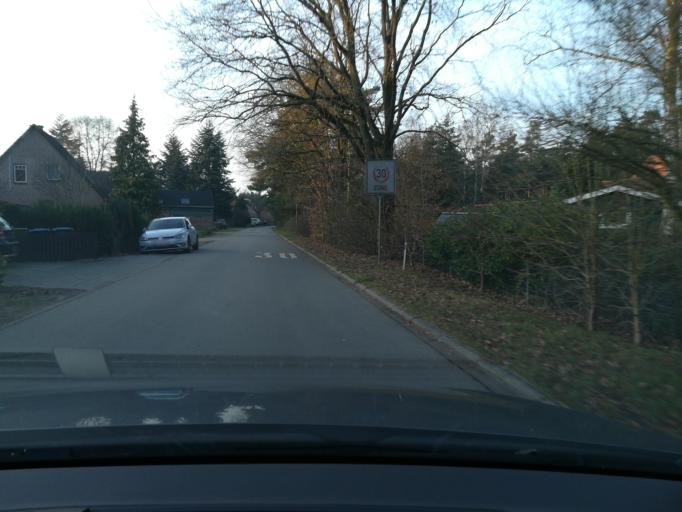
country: DE
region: Schleswig-Holstein
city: Escheburg
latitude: 53.4438
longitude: 10.3100
